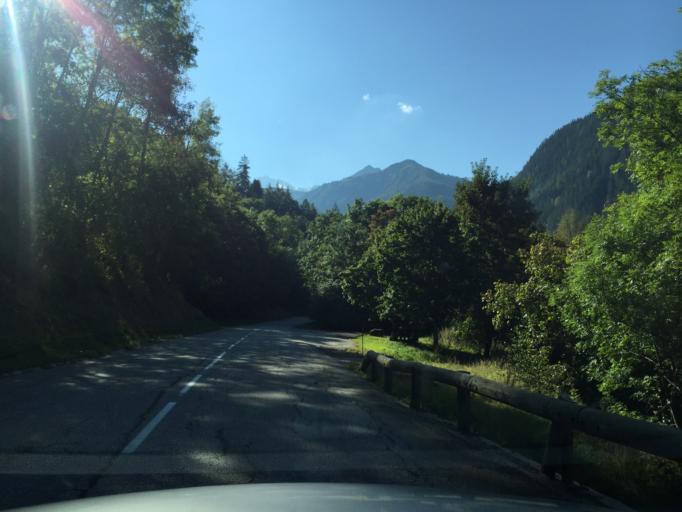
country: FR
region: Rhone-Alpes
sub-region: Departement de la Savoie
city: Belle-Plagne
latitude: 45.5531
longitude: 6.7494
